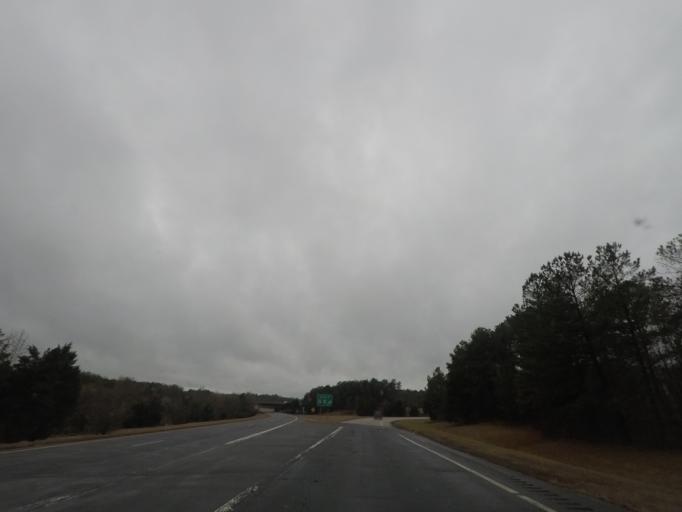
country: US
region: North Carolina
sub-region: Wake County
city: Morrisville
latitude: 35.9036
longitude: -78.8735
